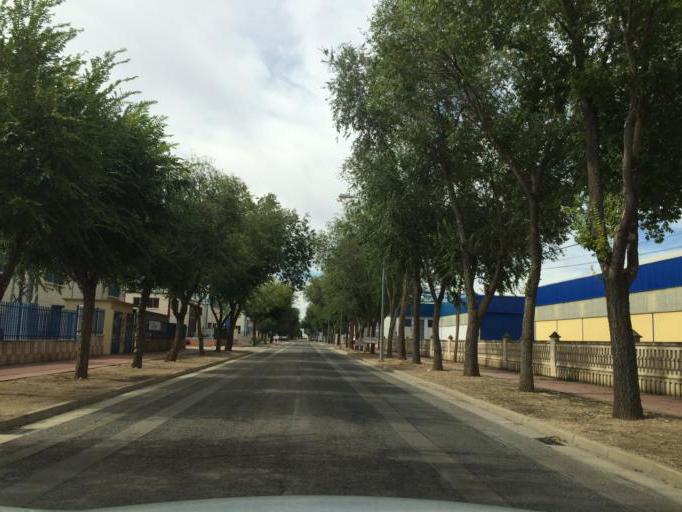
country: ES
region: Castille-La Mancha
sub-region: Provincia de Albacete
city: Albacete
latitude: 39.0174
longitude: -1.8852
